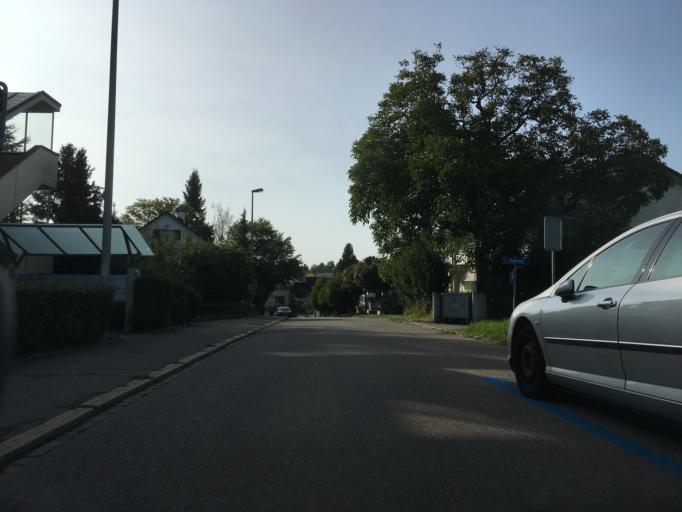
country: CH
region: Zurich
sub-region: Bezirk Buelach
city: Wallisellen / Rieden
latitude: 47.4168
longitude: 8.6005
